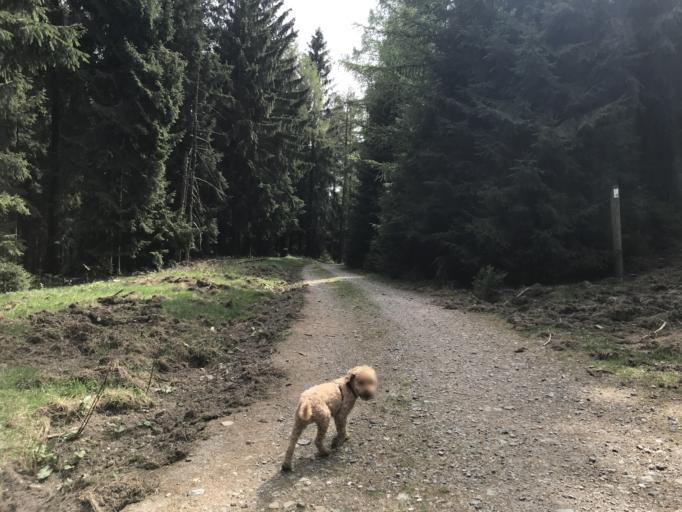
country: DE
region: Hesse
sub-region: Regierungsbezirk Darmstadt
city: Konigstein im Taunus
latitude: 50.2156
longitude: 8.4494
